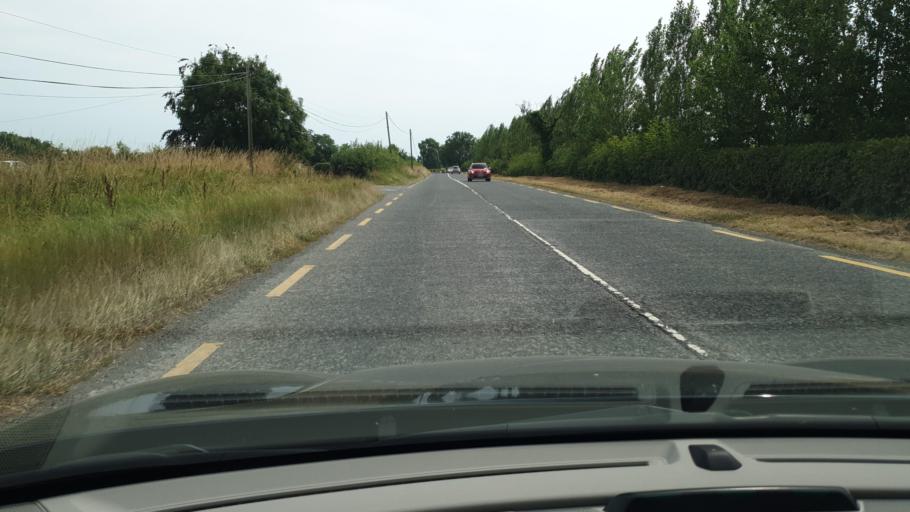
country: IE
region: Leinster
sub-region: An Mhi
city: Navan
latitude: 53.6420
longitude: -6.6199
